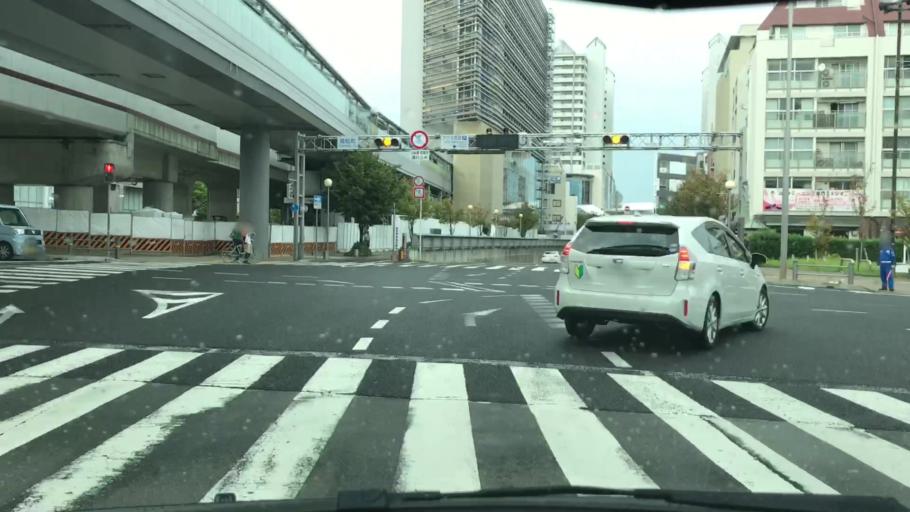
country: JP
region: Hyogo
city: Nishinomiya-hama
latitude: 34.7440
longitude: 135.3578
